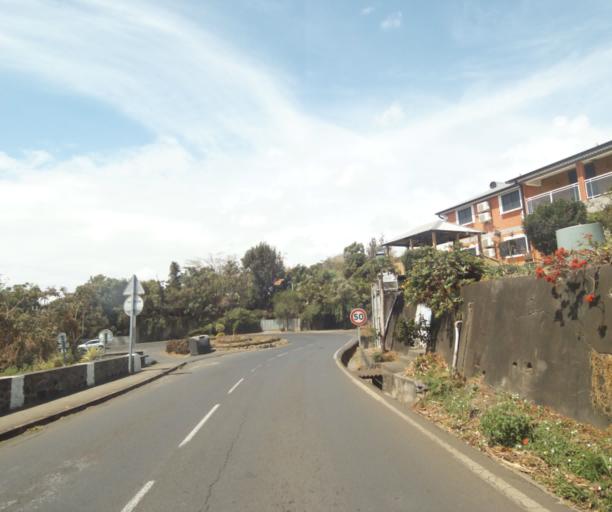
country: RE
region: Reunion
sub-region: Reunion
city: Trois-Bassins
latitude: -21.0774
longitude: 55.2689
